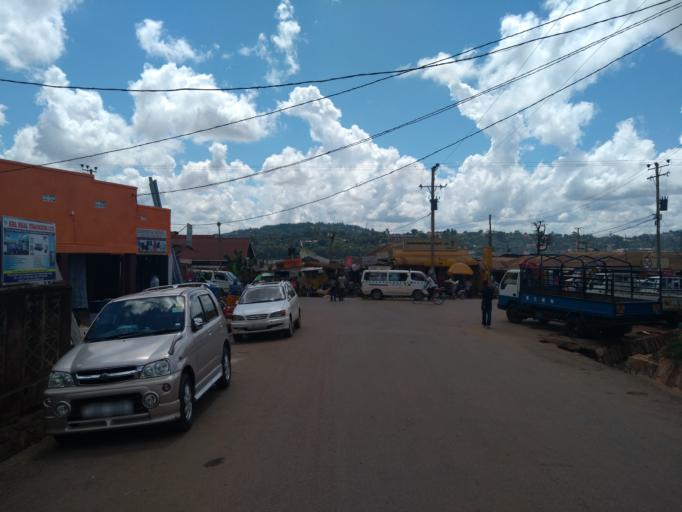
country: UG
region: Central Region
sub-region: Kampala District
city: Kampala
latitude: 0.3043
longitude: 32.6138
